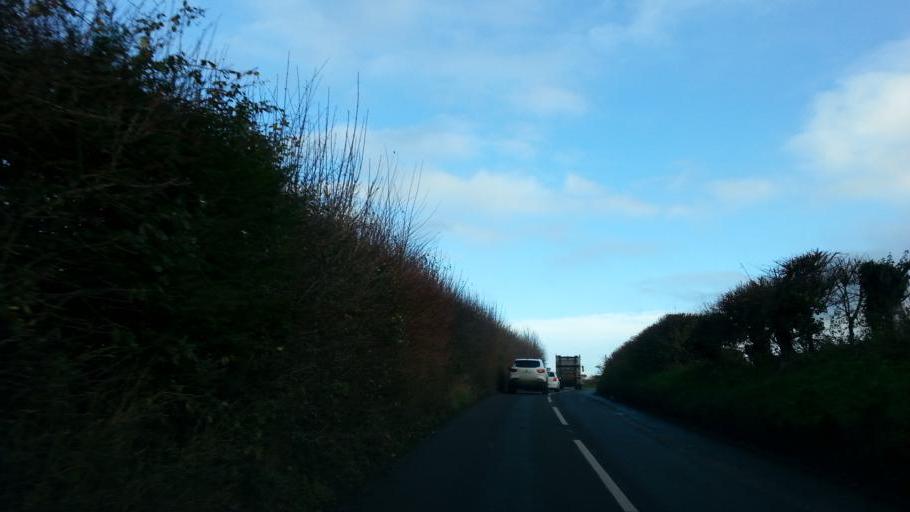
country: GB
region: England
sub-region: Oxfordshire
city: Faringdon
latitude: 51.6250
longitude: -1.5760
